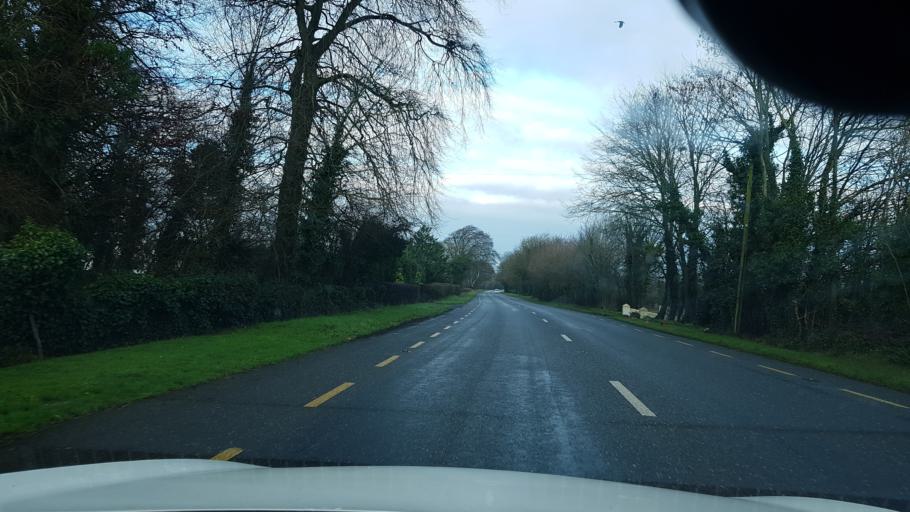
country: IE
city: Kentstown
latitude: 53.5808
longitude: -6.5882
